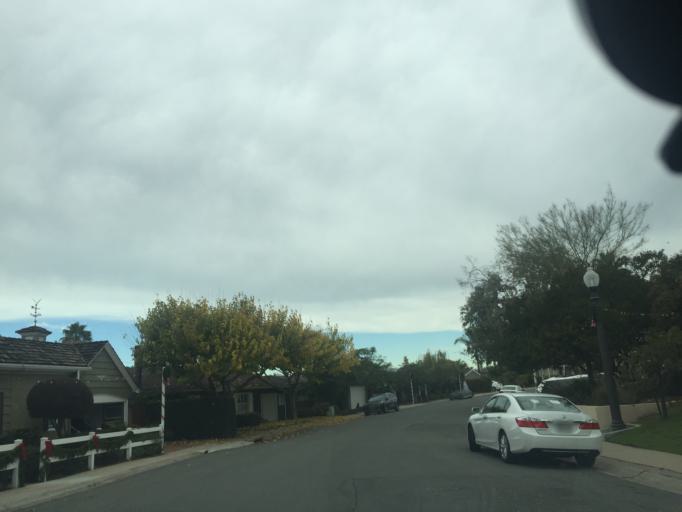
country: US
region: California
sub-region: San Diego County
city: Lemon Grove
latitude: 32.7644
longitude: -117.0903
